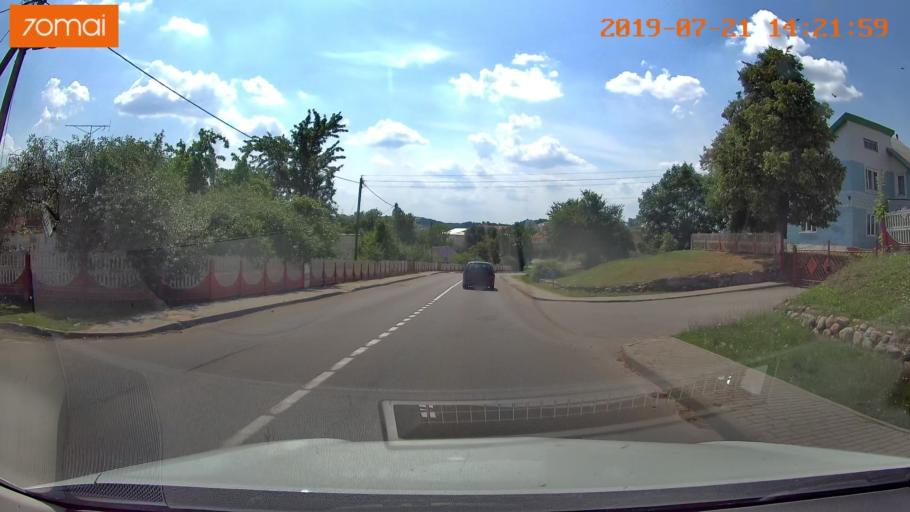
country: BY
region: Grodnenskaya
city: Karelichy
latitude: 53.5743
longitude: 26.1409
